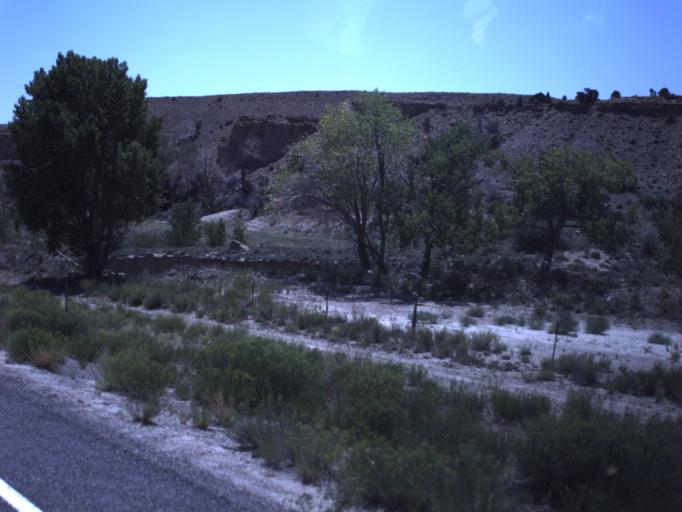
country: US
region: Utah
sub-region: Emery County
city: Orangeville
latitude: 39.2352
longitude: -111.0852
